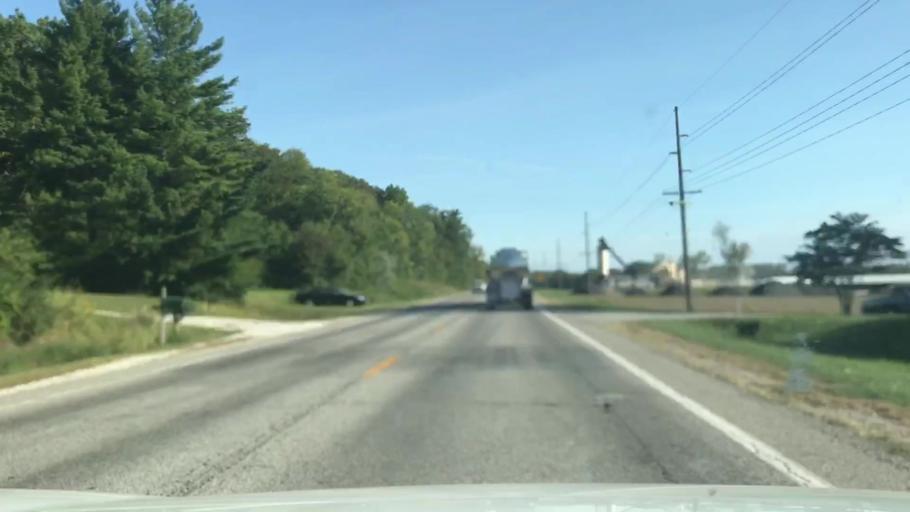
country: US
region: Illinois
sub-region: Adams County
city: Quincy
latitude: 39.8521
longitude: -91.3811
